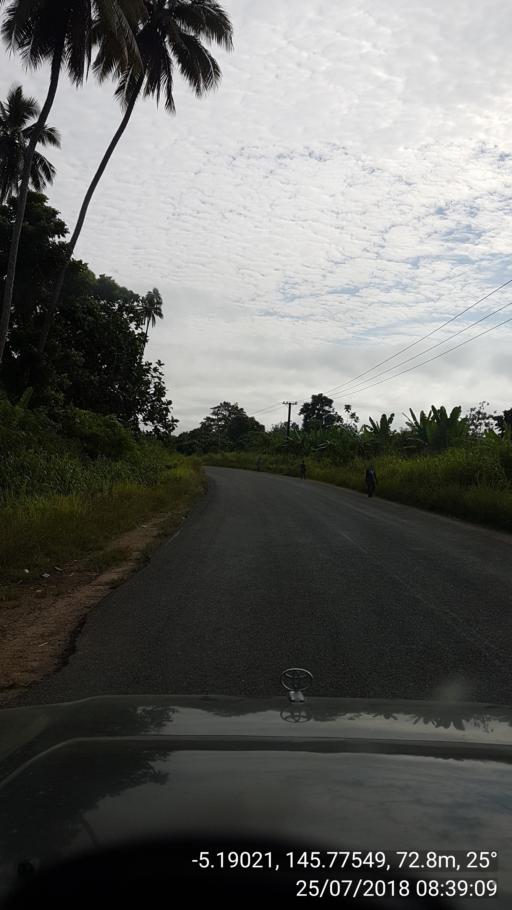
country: PG
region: Madang
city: Madang
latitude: -5.1903
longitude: 145.7756
